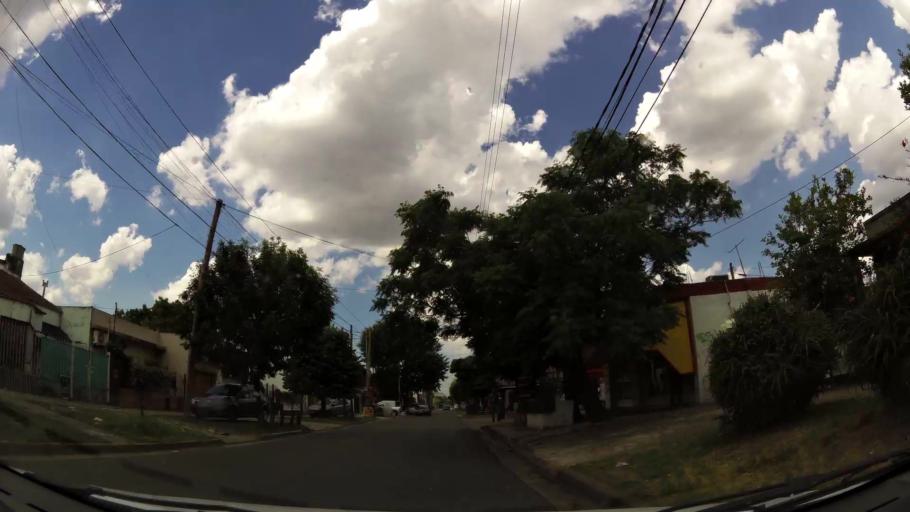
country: AR
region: Buenos Aires
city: Ituzaingo
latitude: -34.6497
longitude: -58.6689
